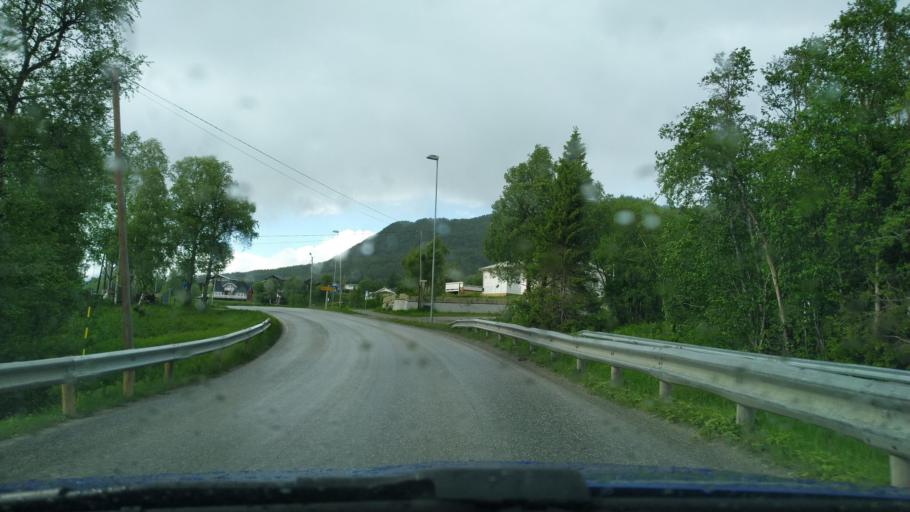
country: NO
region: Troms
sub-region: Sorreisa
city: Sorreisa
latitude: 69.1509
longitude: 18.1704
